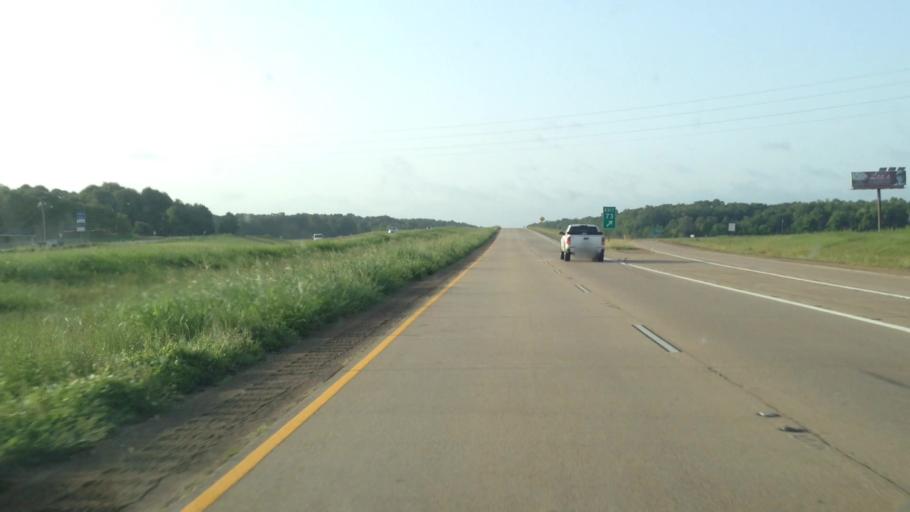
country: US
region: Louisiana
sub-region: Rapides Parish
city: Woodworth
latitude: 31.1692
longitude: -92.4625
